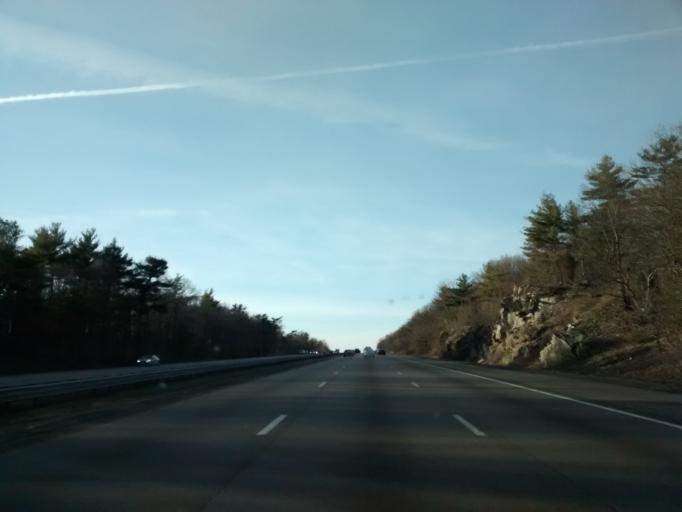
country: US
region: Massachusetts
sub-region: Norfolk County
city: Randolph
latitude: 42.1693
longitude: -71.0723
